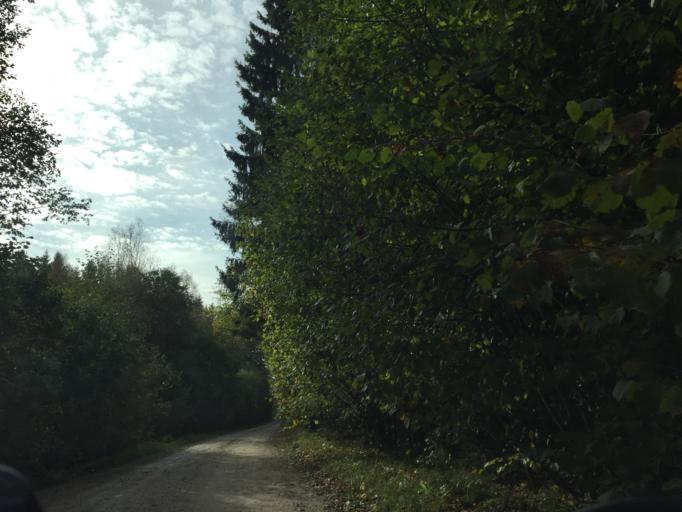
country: LV
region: Jaunpils
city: Jaunpils
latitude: 56.6132
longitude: 23.0164
